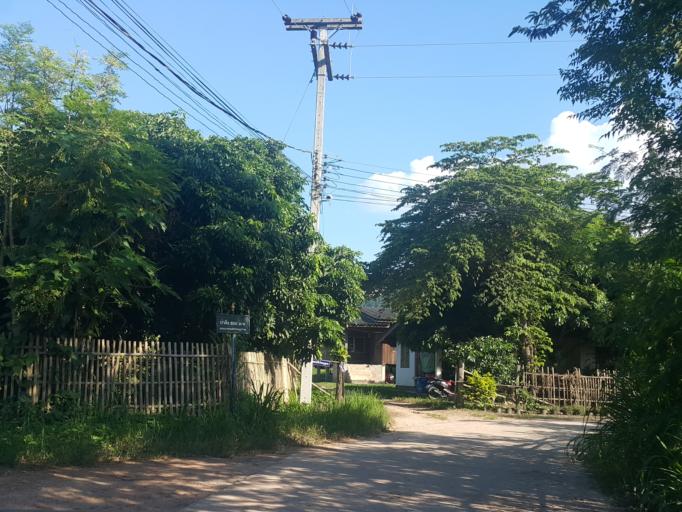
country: TH
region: Chiang Mai
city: Mae On
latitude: 18.7175
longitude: 99.2092
